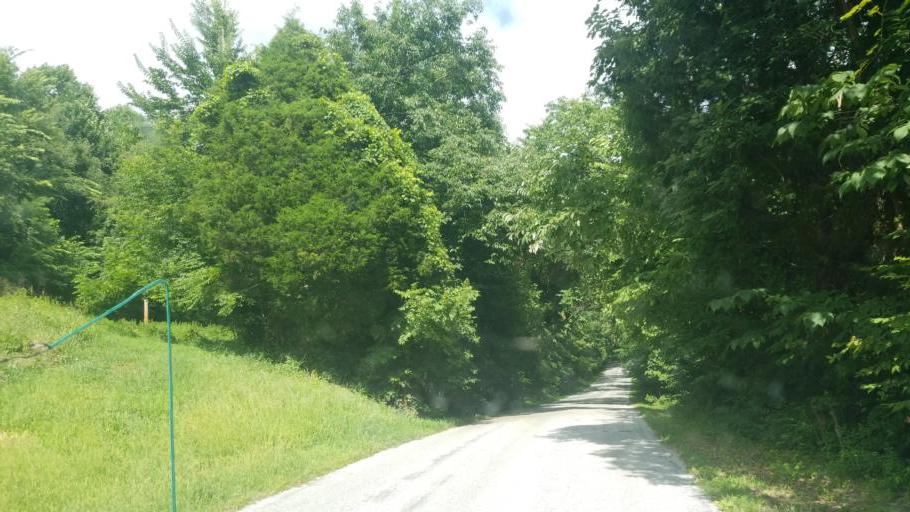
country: US
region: Illinois
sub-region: Union County
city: Cobden
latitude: 37.6095
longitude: -89.3588
